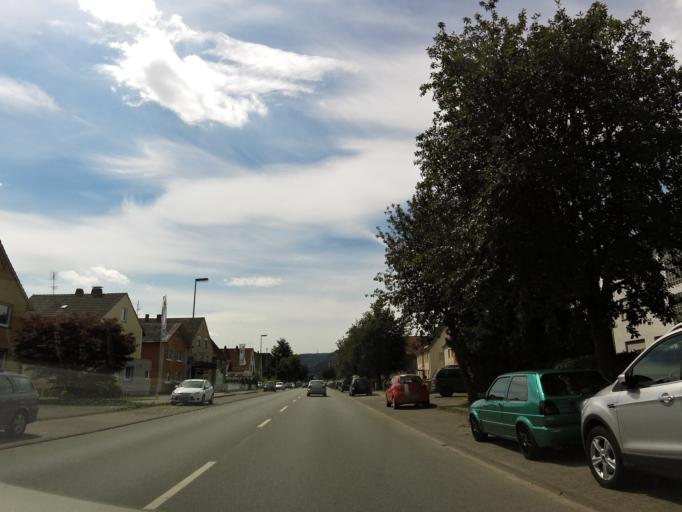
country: DE
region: North Rhine-Westphalia
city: Beverungen
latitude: 51.6718
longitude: 9.3752
